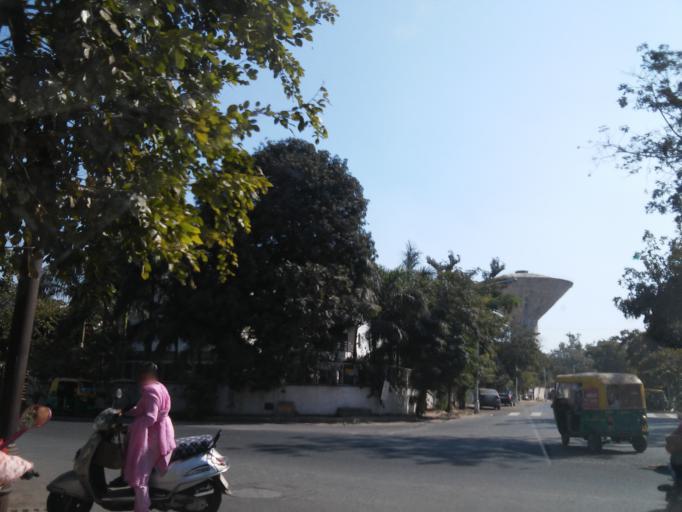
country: IN
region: Gujarat
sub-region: Ahmadabad
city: Ahmedabad
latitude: 23.0177
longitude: 72.5423
